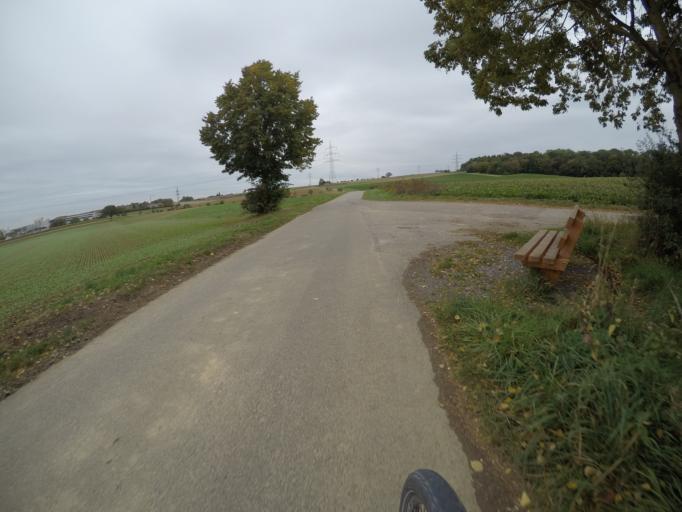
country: DE
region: Baden-Wuerttemberg
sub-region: Regierungsbezirk Stuttgart
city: Leonberg
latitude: 48.8362
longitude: 8.9938
